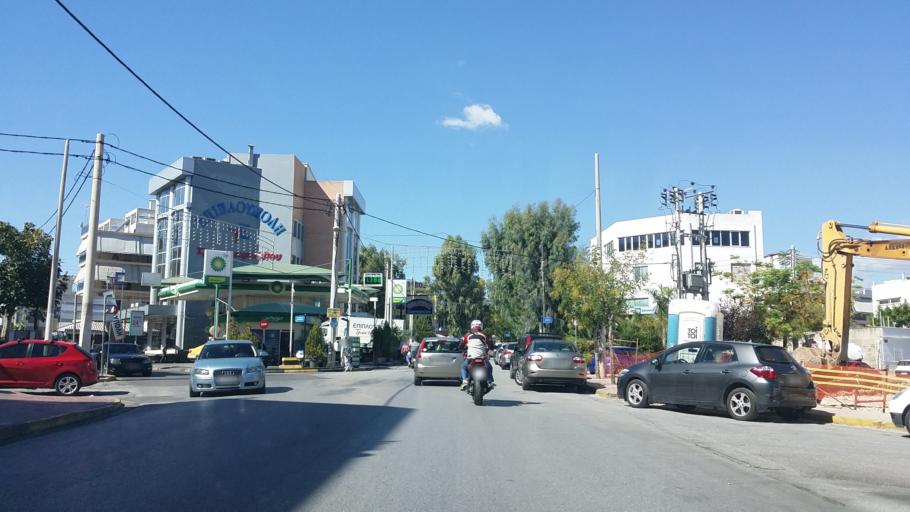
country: GR
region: Attica
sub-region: Nomarchia Athinas
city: Ilion
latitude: 38.0317
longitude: 23.7107
